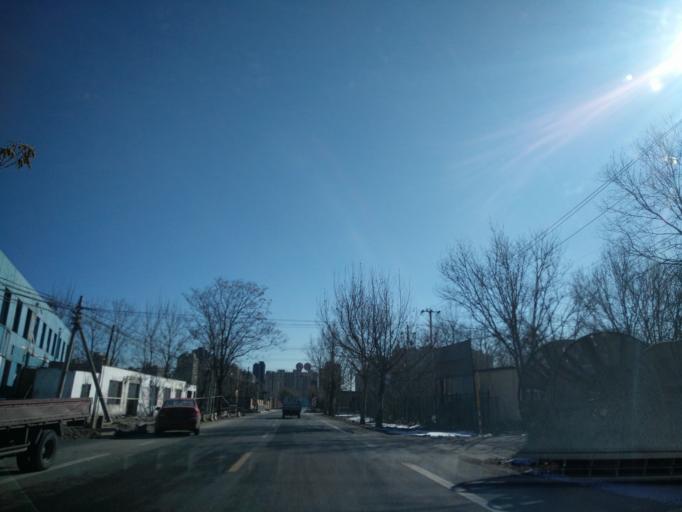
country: CN
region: Beijing
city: Yinghai
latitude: 39.7526
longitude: 116.4710
